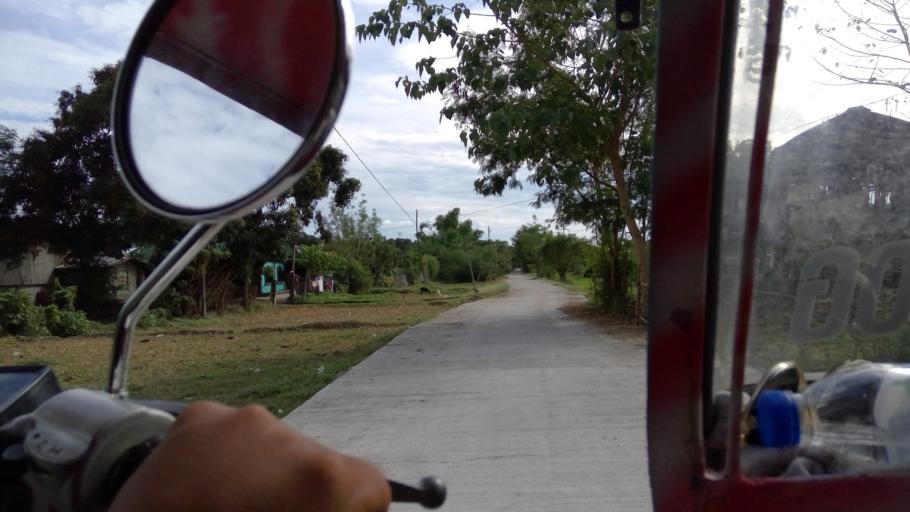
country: PH
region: Ilocos
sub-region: Province of La Union
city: San Eugenio
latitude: 16.3643
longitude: 120.3525
